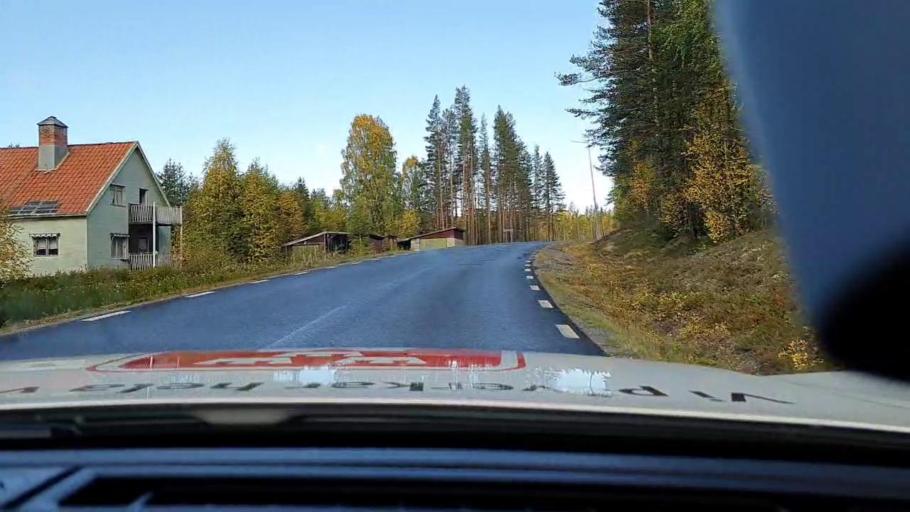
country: SE
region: Vaesterbotten
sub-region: Skelleftea Kommun
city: Langsele
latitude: 64.9479
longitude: 20.0220
